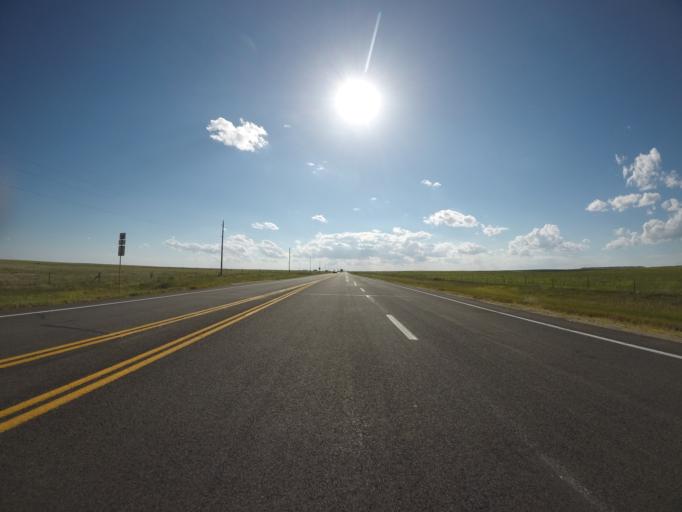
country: US
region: Colorado
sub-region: Morgan County
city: Fort Morgan
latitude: 40.6113
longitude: -103.8051
